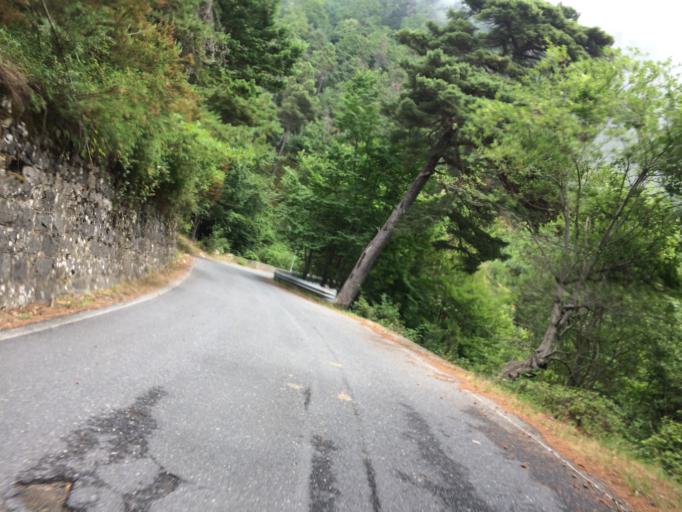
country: IT
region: Liguria
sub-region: Provincia di Imperia
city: Ceriana
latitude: 43.8651
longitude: 7.7469
